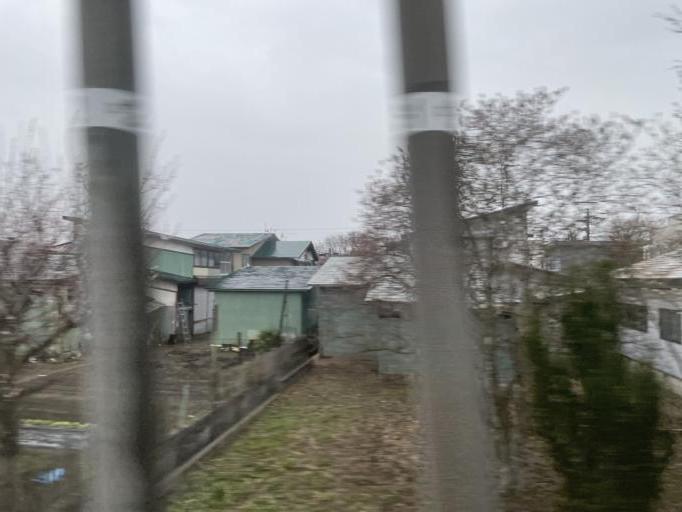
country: JP
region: Akita
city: Kakunodatemachi
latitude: 39.5487
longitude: 140.5437
